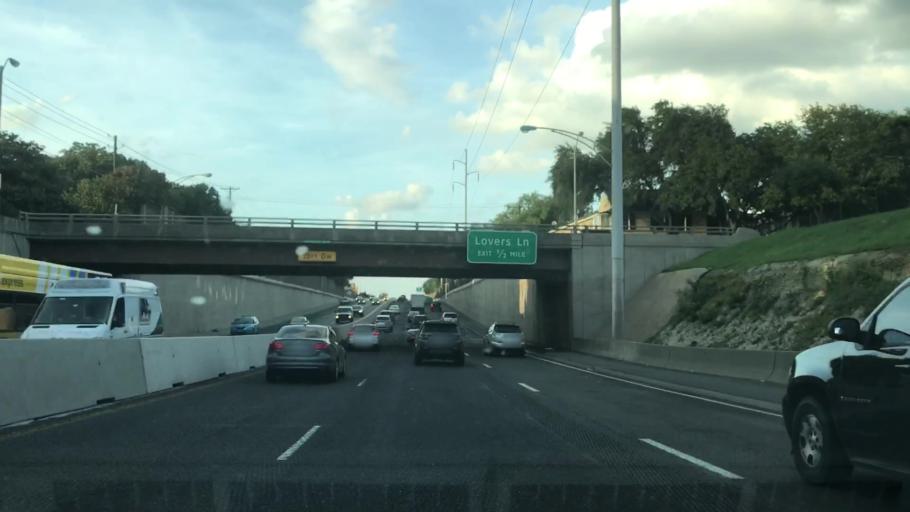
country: US
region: Texas
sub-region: Dallas County
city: University Park
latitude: 32.8449
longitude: -96.8139
